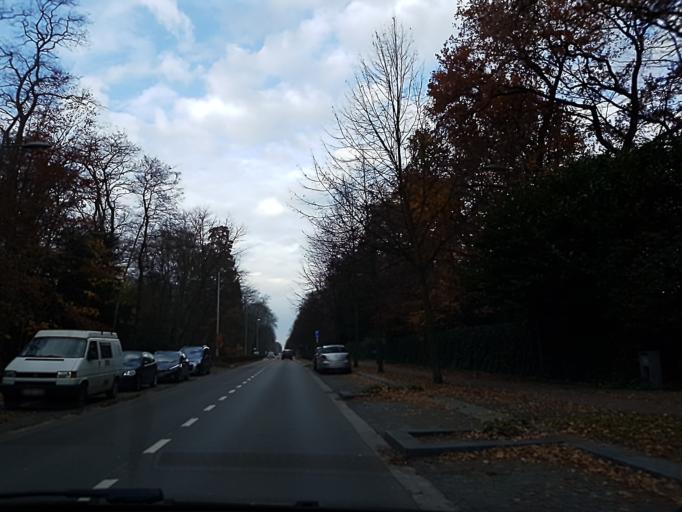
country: BE
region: Flanders
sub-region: Provincie Antwerpen
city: Kapellen
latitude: 51.3203
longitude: 4.4244
